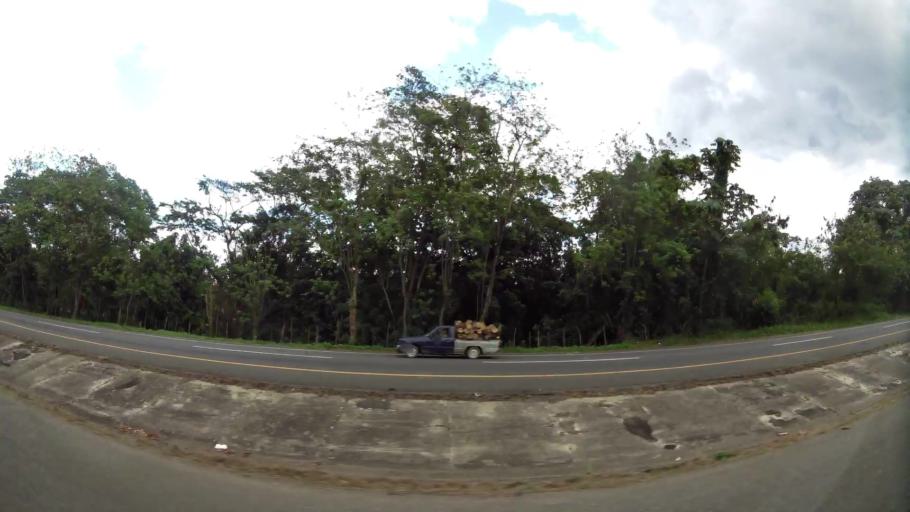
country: DO
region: Monsenor Nouel
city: Sabana del Puerto
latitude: 19.0759
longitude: -70.4458
